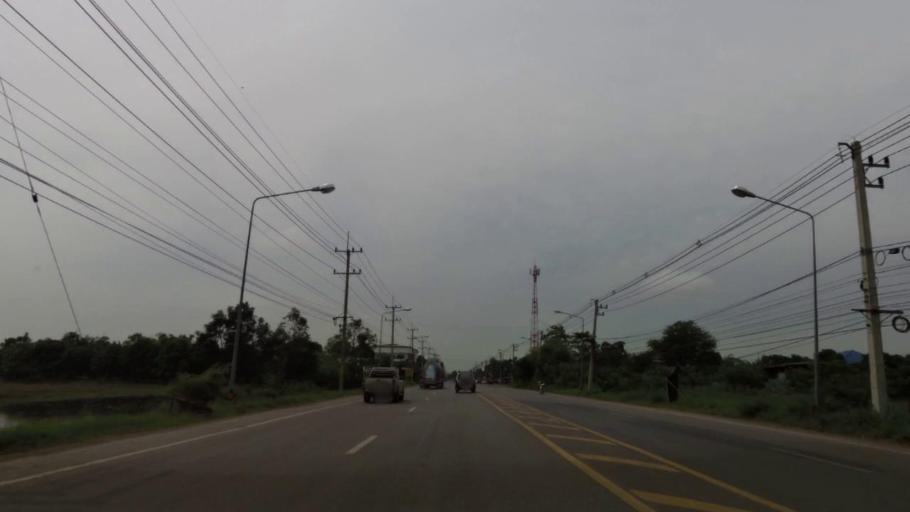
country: TH
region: Lop Buri
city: Ban Mi
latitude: 15.0543
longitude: 100.5817
